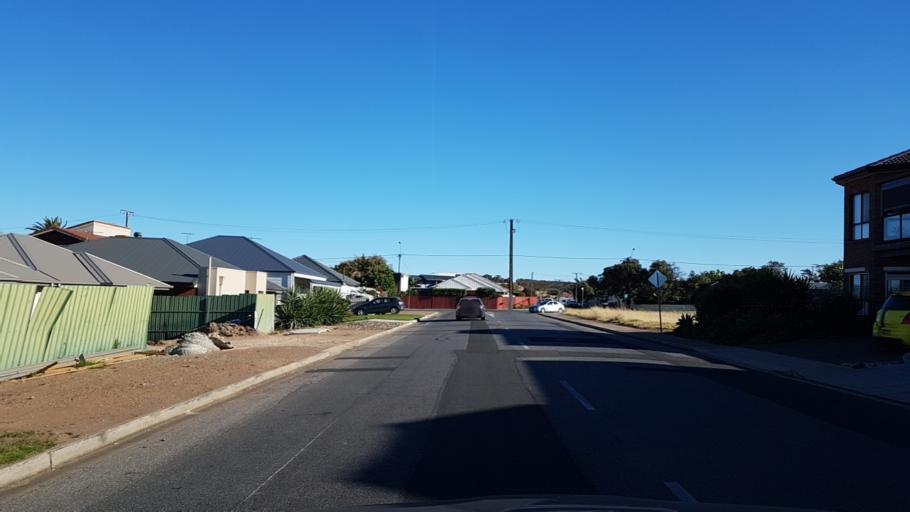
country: AU
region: South Australia
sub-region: Adelaide
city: Port Noarlunga
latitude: -35.1319
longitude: 138.4731
